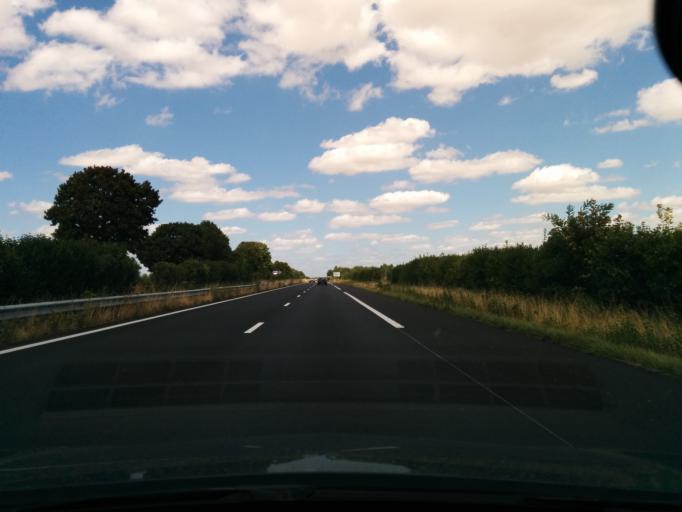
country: FR
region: Centre
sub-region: Departement de l'Indre
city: Montierchaume
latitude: 46.9594
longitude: 1.7592
